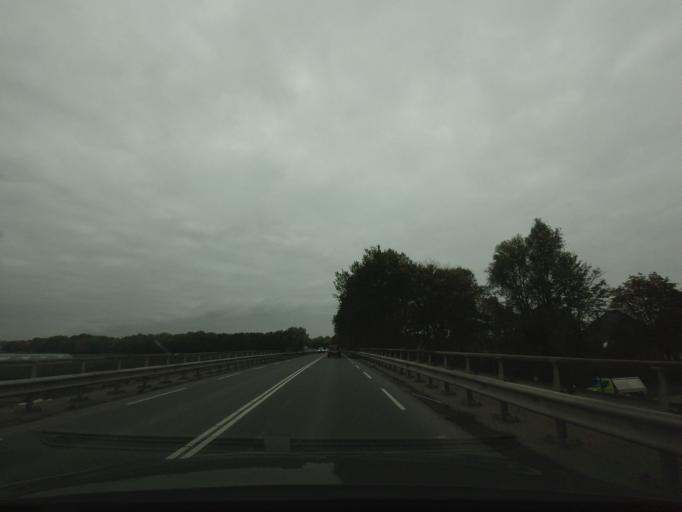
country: NL
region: North Holland
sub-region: Gemeente Heerhugowaard
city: Heerhugowaard
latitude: 52.6755
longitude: 4.8739
